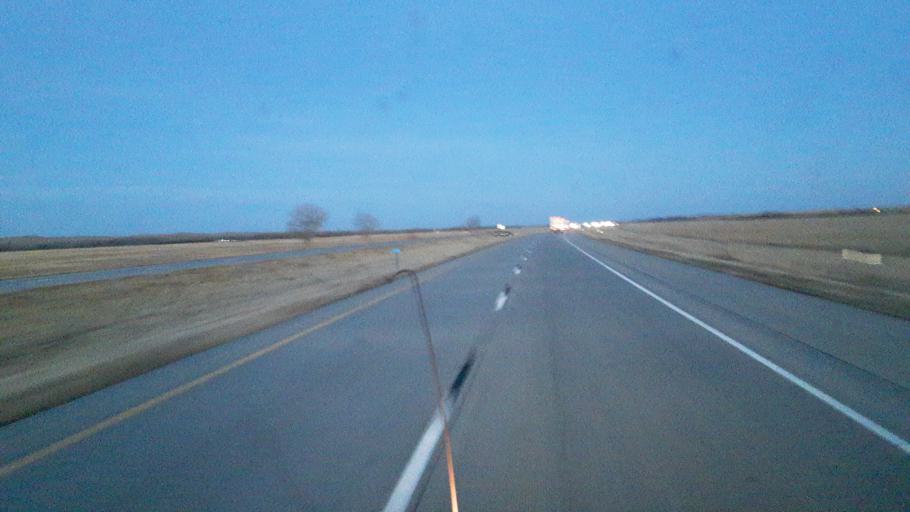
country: US
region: Nebraska
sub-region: Keith County
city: Ogallala
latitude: 41.1091
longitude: -101.4389
